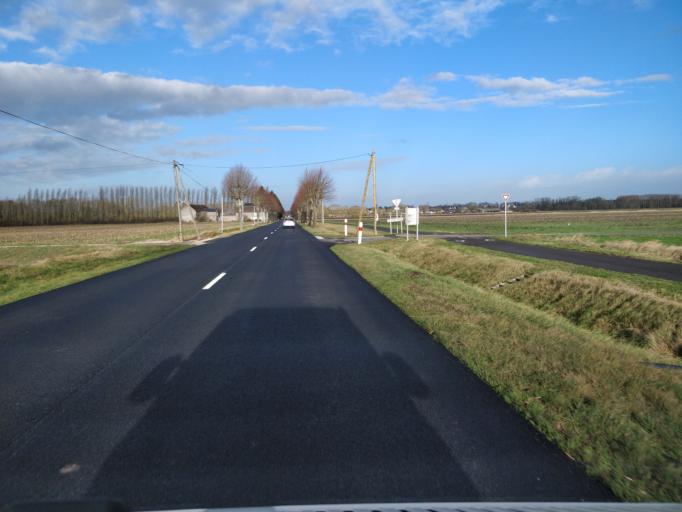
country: FR
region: Centre
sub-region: Departement du Loir-et-Cher
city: Muides-sur-Loire
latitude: 47.6819
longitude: 1.5210
